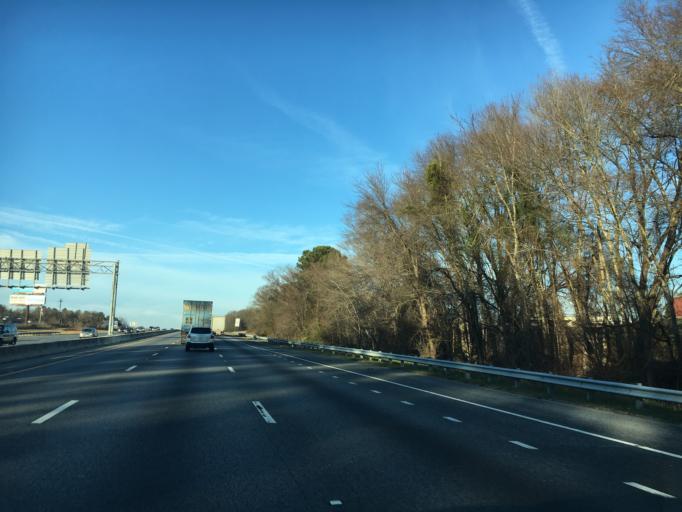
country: US
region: South Carolina
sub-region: Anderson County
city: Piedmont
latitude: 34.7002
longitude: -82.5020
